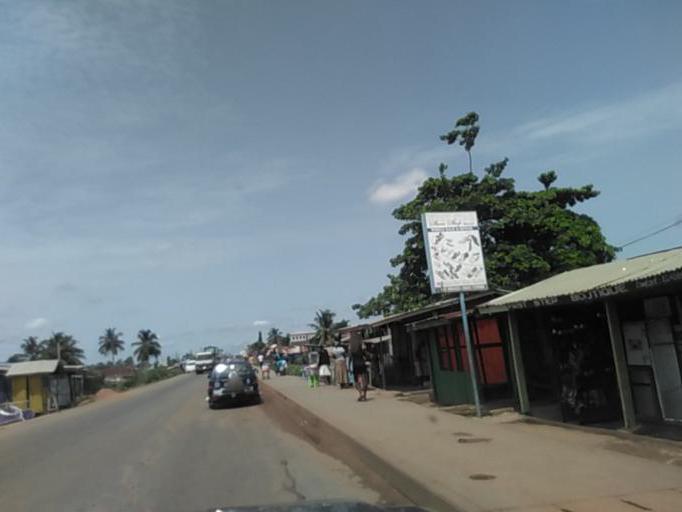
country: GH
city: Akropong
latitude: 6.1586
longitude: 0.0629
